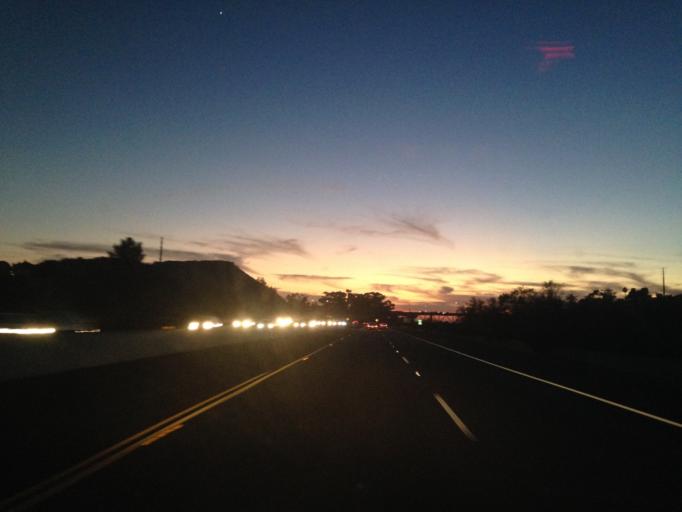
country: US
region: California
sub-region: San Diego County
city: Oceanside
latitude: 33.2101
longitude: -117.3785
